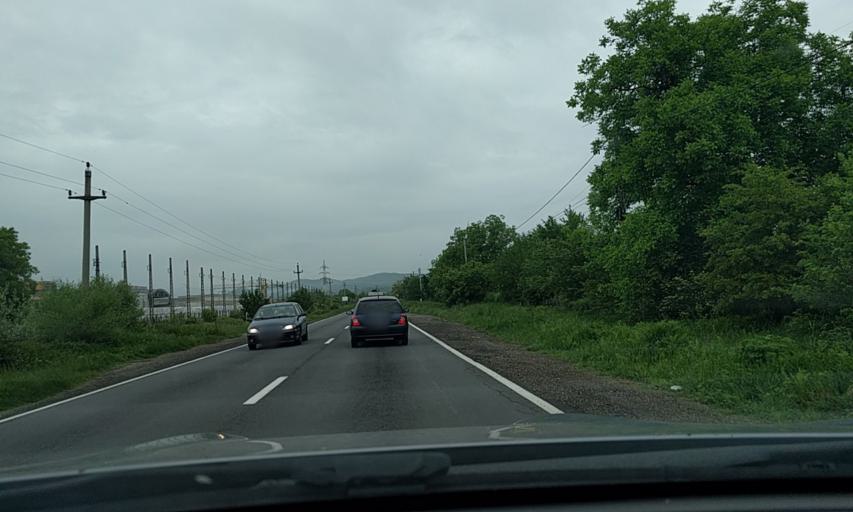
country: RO
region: Dambovita
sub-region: Comuna Vulcana-Pandele
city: Vulcana-Pandele
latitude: 45.0049
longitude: 25.4015
